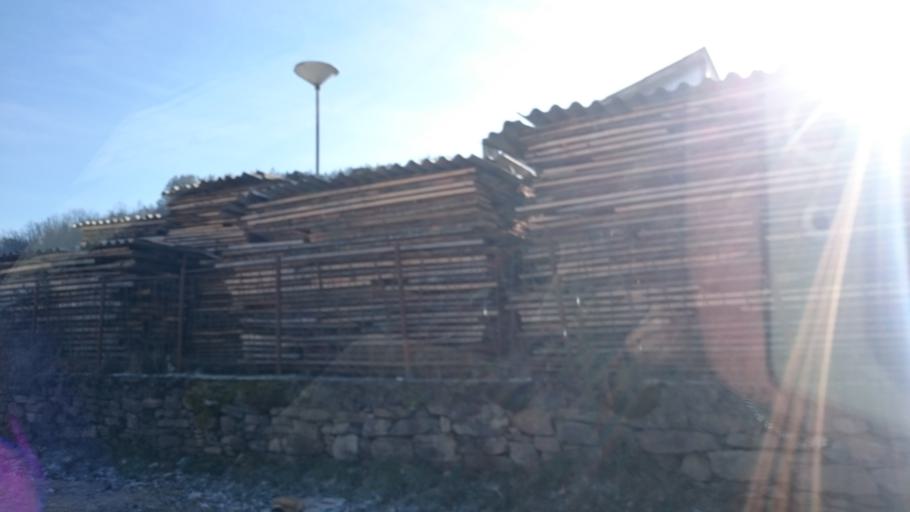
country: MK
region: Makedonski Brod
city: Makedonski Brod
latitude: 41.5075
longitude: 21.2206
